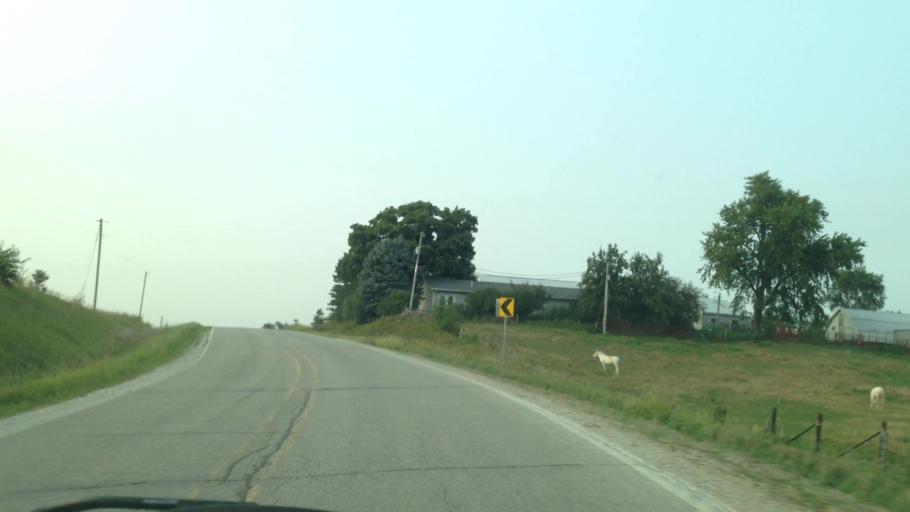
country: US
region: Iowa
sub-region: Iowa County
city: Marengo
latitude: 41.8645
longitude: -92.0888
